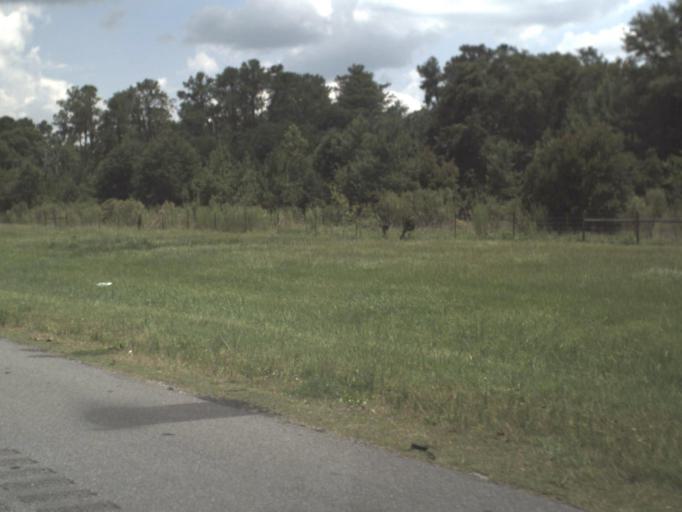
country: US
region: Florida
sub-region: Suwannee County
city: Wellborn
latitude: 30.3667
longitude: -82.8558
